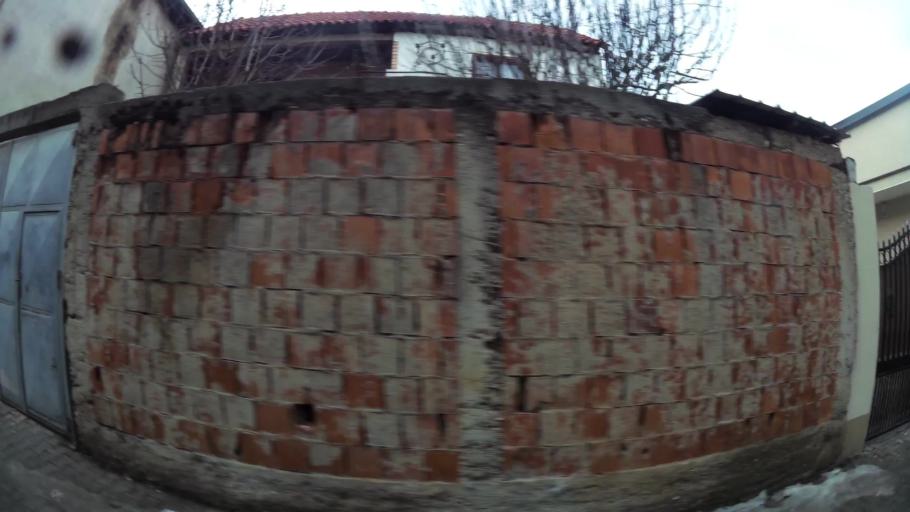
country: XK
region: Pristina
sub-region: Komuna e Prishtines
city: Pristina
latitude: 42.6763
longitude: 21.1667
